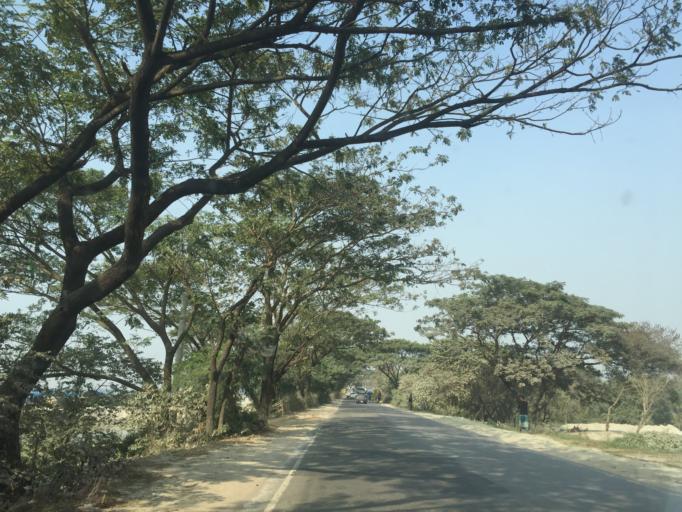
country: BD
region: Dhaka
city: Tungi
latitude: 23.8338
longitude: 90.3401
